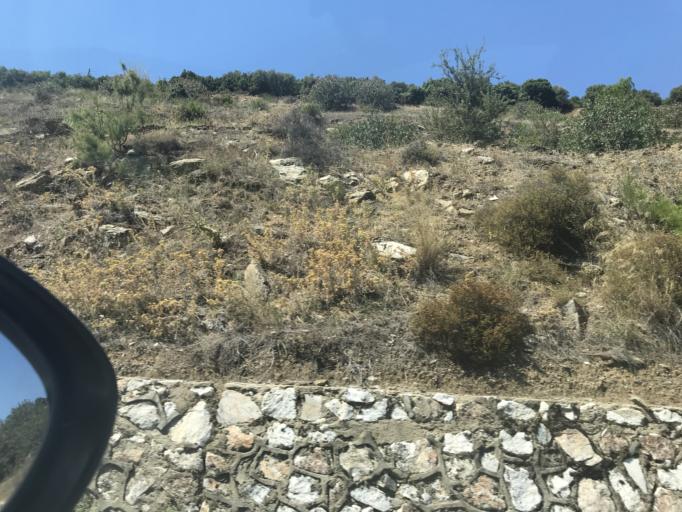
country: TR
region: Aydin
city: Akcaova
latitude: 37.5066
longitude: 28.1023
